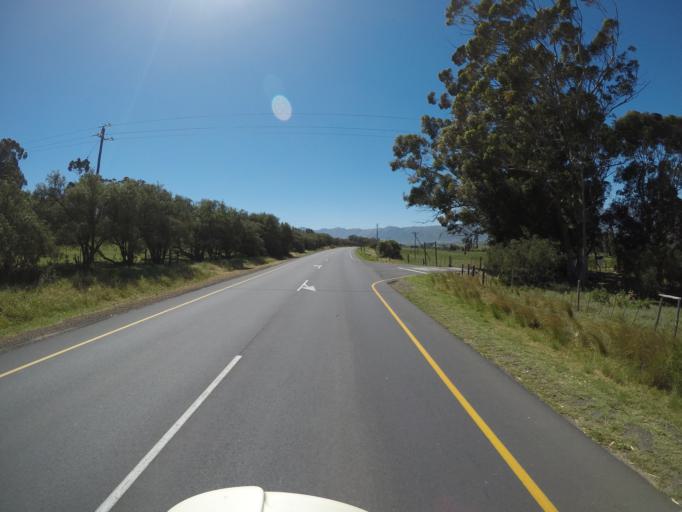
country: ZA
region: Western Cape
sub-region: Cape Winelands District Municipality
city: Ceres
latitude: -33.3162
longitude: 19.0922
